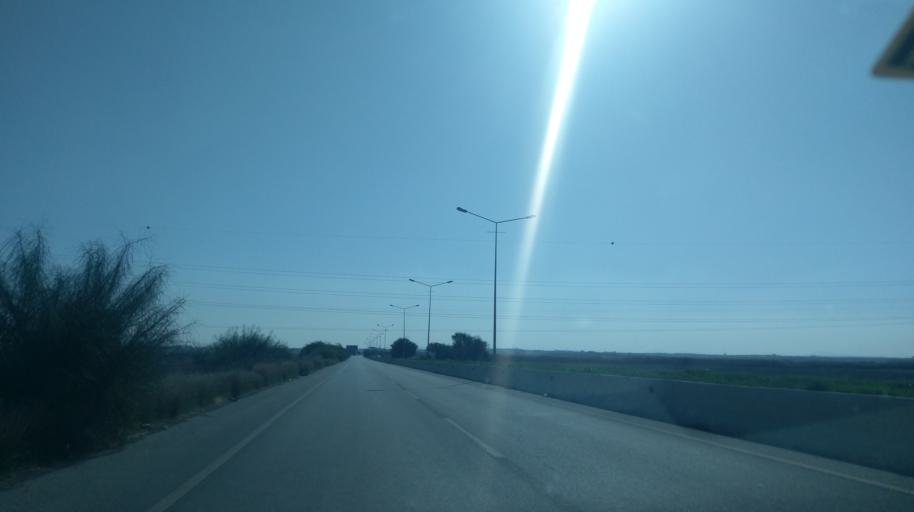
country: CY
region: Lefkosia
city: Geri
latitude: 35.1946
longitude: 33.5013
